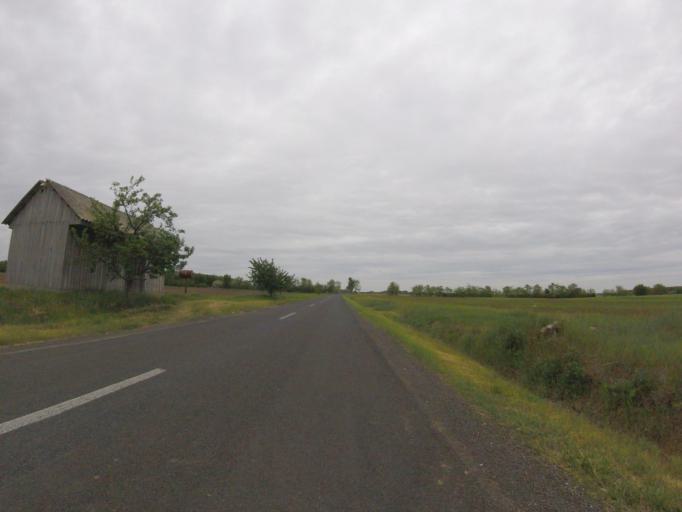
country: HU
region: Pest
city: Ujhartyan
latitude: 47.1847
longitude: 19.3594
